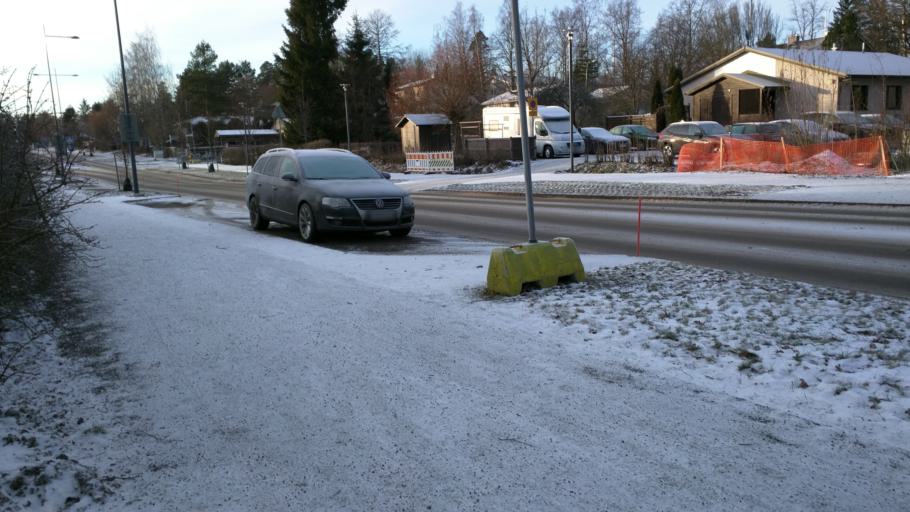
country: FI
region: Uusimaa
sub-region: Helsinki
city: Kilo
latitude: 60.2448
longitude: 24.7565
